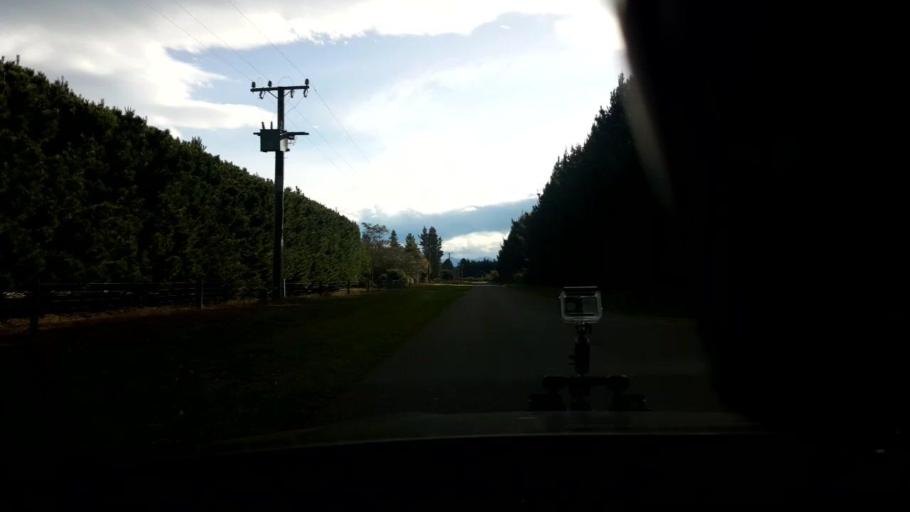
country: NZ
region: Canterbury
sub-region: Waimakariri District
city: Oxford
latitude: -43.3974
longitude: 172.3097
